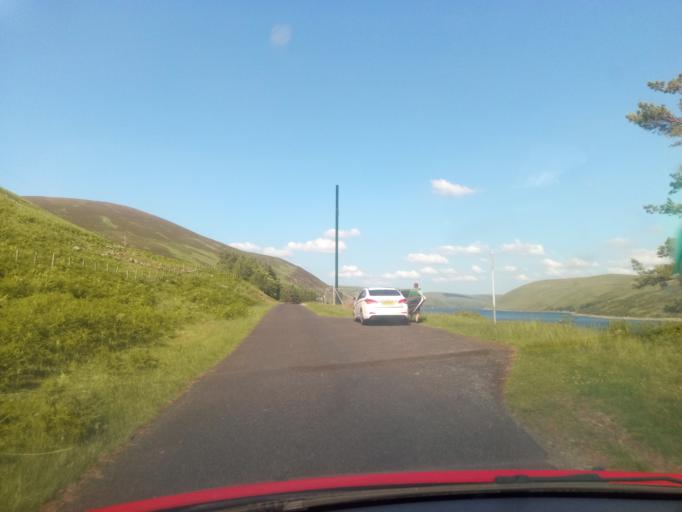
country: GB
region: Scotland
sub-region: Dumfries and Galloway
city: Moffat
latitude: 55.4800
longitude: -3.3077
